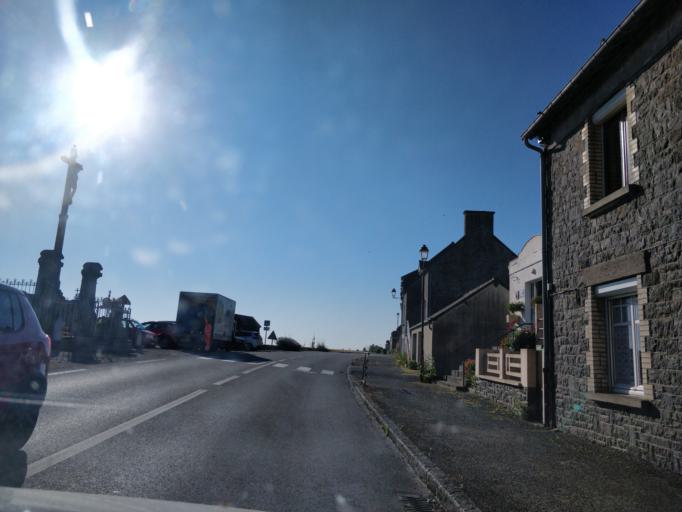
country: FR
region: Brittany
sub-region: Departement d'Ille-et-Vilaine
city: La Fresnais
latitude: 48.6145
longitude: -1.8411
